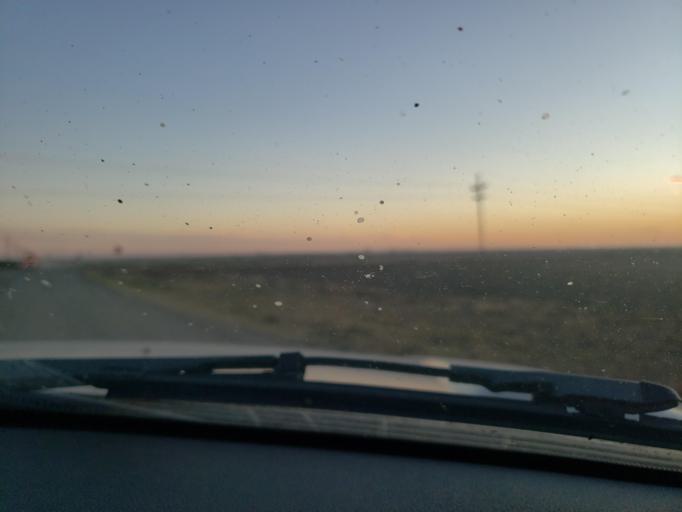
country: US
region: Kansas
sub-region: Finney County
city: Garden City
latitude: 37.9900
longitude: -100.8107
